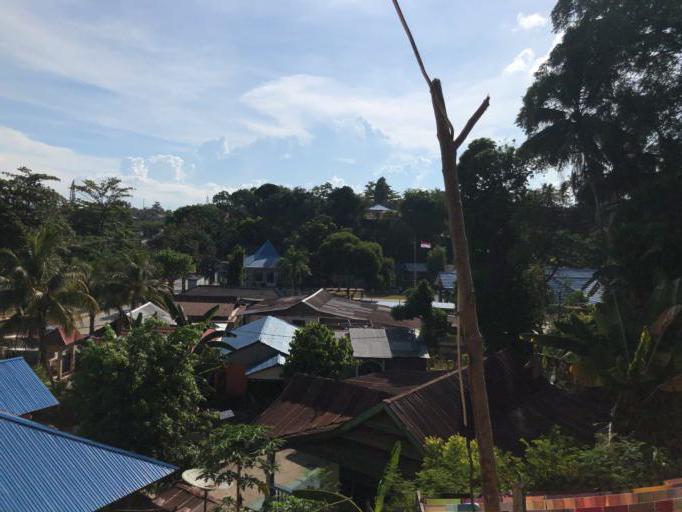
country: ID
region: Sulawesi Tenggara
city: Kendari
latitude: -3.9710
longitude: 122.6029
